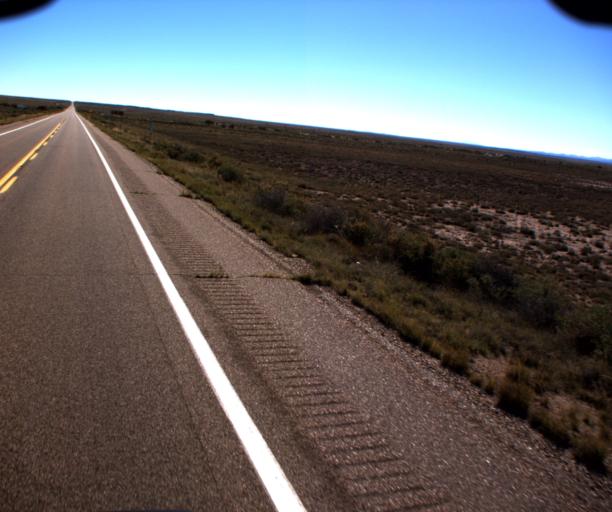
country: US
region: Arizona
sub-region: Navajo County
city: Holbrook
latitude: 34.7906
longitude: -109.8900
